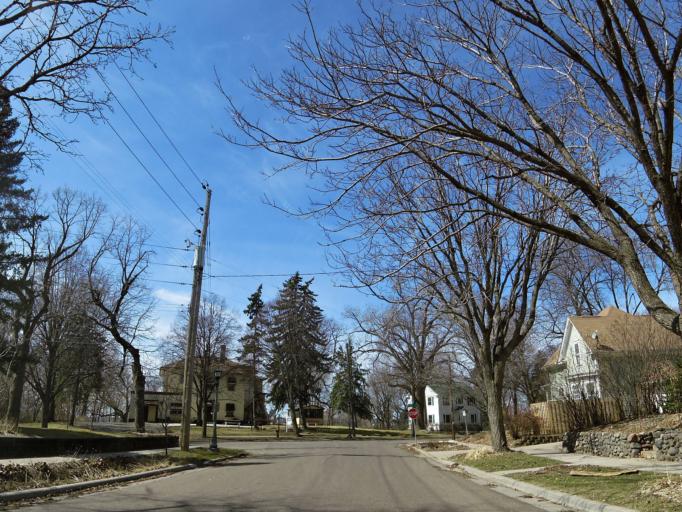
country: US
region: Minnesota
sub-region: Ramsey County
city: Saint Paul
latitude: 44.9488
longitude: -93.0600
